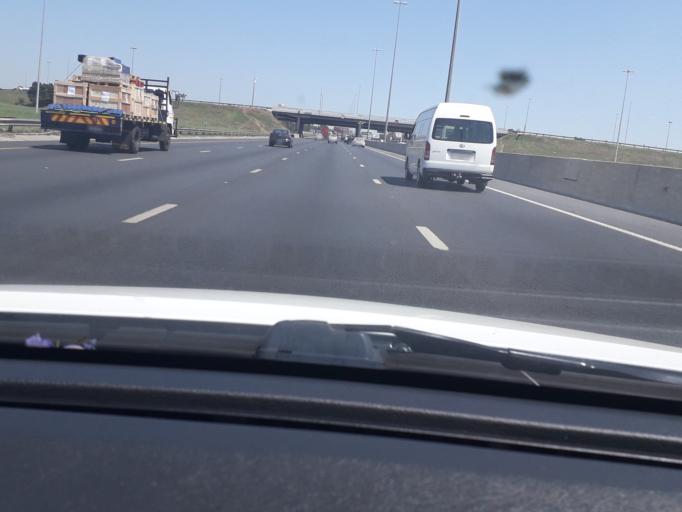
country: ZA
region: Gauteng
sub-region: Ekurhuleni Metropolitan Municipality
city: Germiston
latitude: -26.1771
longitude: 28.2004
